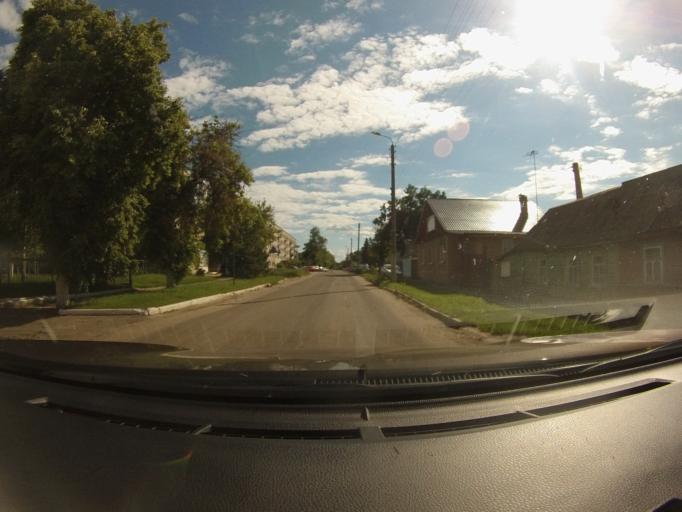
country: RU
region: Orjol
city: Mtsensk
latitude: 53.2832
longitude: 36.5716
